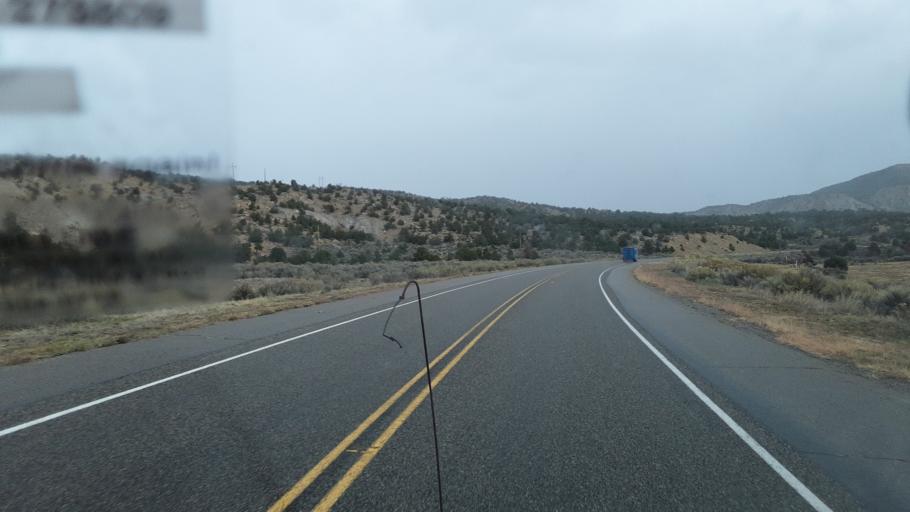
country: US
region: New Mexico
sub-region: Rio Arriba County
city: Santa Teresa
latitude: 36.3837
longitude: -106.5036
